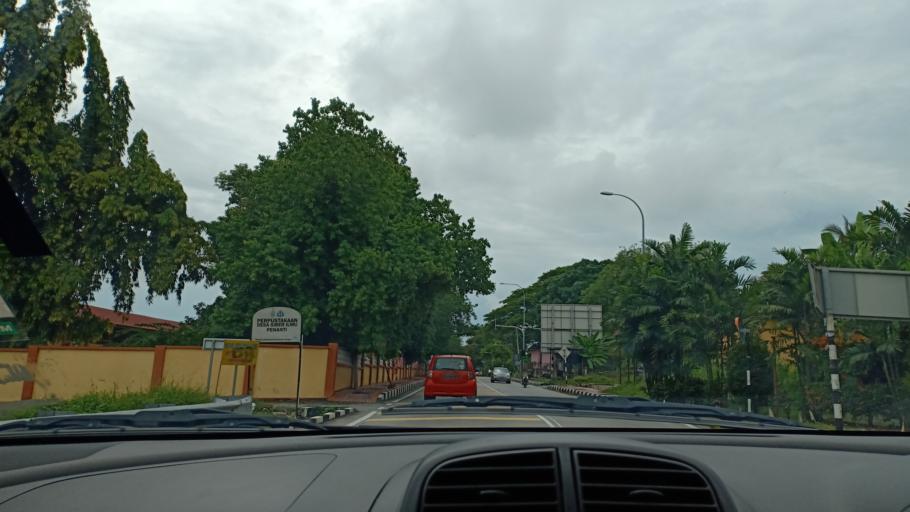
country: MY
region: Penang
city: Bukit Mertajam
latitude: 5.4059
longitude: 100.4699
